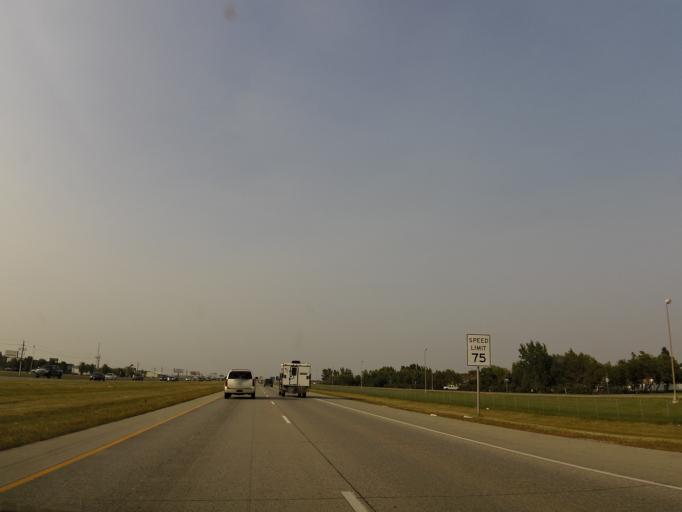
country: US
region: North Dakota
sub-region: Cass County
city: Fargo
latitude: 46.8132
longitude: -96.8390
